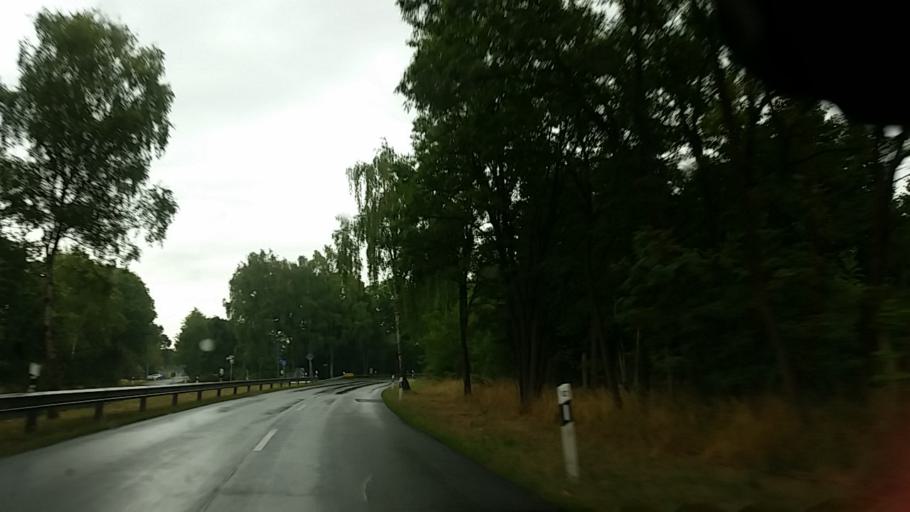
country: DE
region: Lower Saxony
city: Bokensdorf
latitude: 52.5403
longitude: 10.7170
